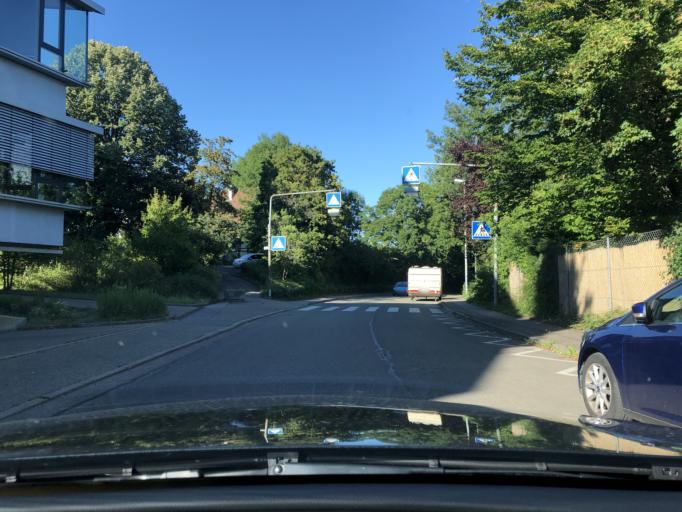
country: DE
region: Baden-Wuerttemberg
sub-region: Regierungsbezirk Stuttgart
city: Weinstadt-Endersbach
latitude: 48.7923
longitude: 9.3430
